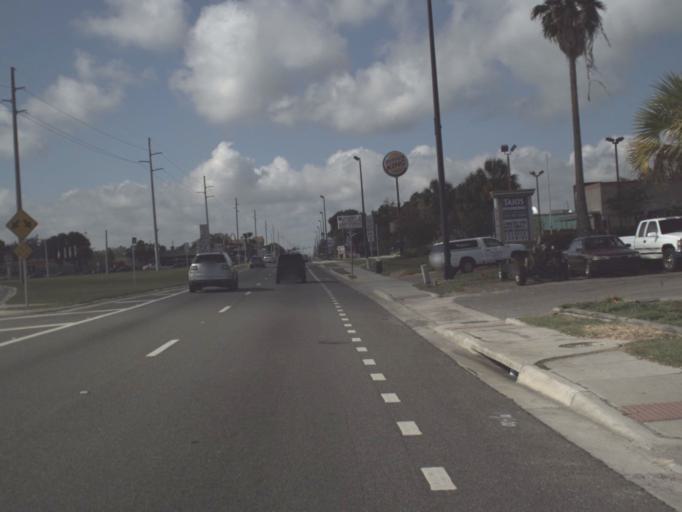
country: US
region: Florida
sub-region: Lake County
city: Leesburg
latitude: 28.8276
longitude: -81.8875
